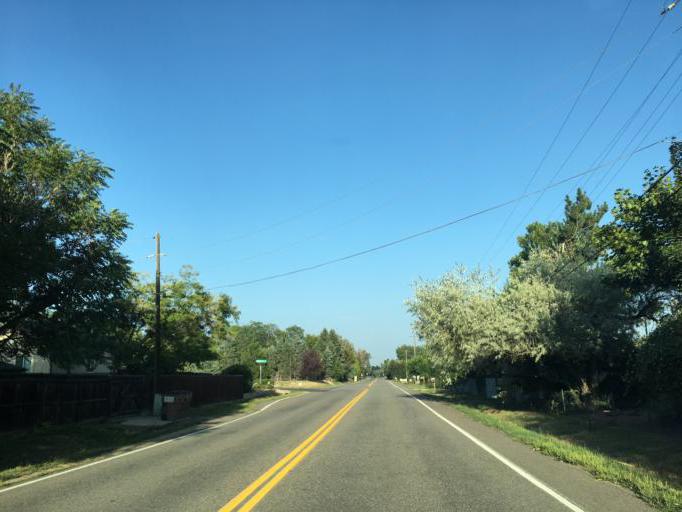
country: US
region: Colorado
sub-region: Jefferson County
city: Applewood
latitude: 39.7907
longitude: -105.1704
